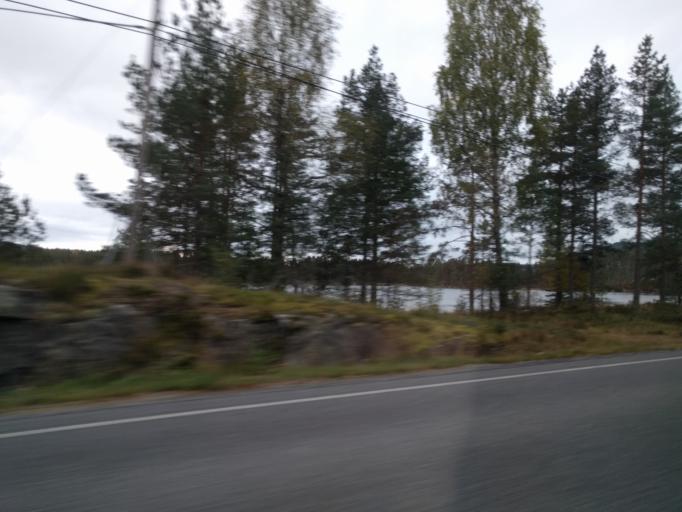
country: NO
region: Aust-Agder
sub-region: Evje og Hornnes
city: Evje
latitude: 58.5186
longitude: 7.7737
